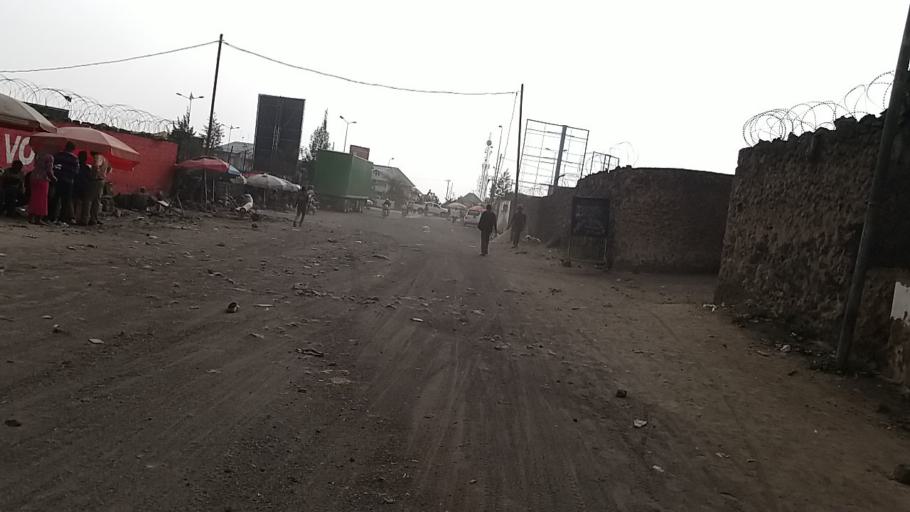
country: CD
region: Nord Kivu
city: Goma
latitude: -1.6833
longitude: 29.2363
